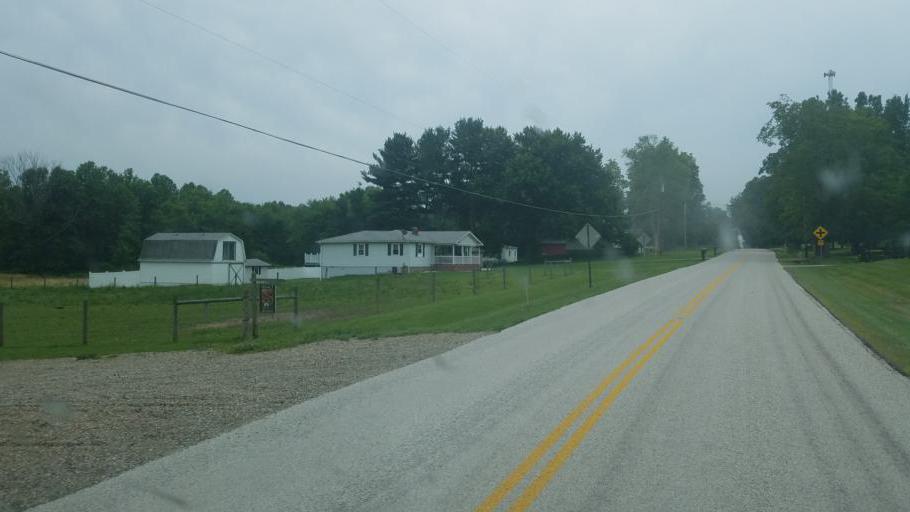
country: US
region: Ohio
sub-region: Trumbull County
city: South Canal
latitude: 41.1547
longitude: -81.0512
